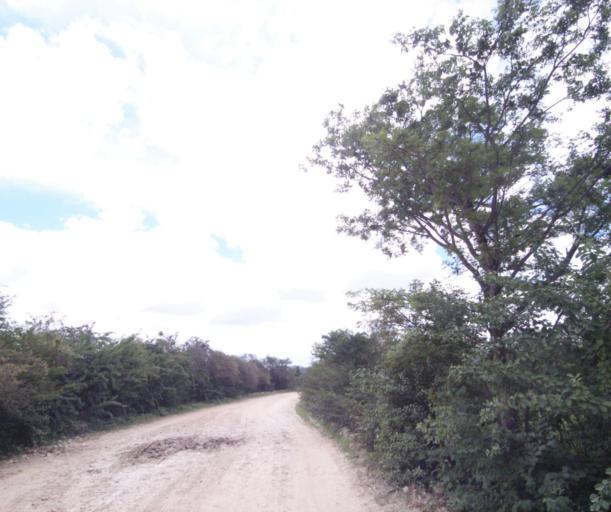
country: BR
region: Bahia
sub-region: Tanhacu
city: Tanhacu
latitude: -14.1694
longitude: -41.1389
